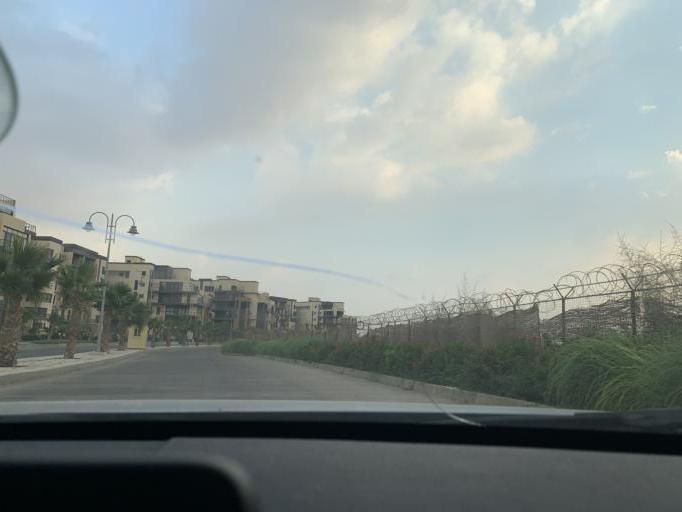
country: EG
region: Muhafazat al Qalyubiyah
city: Al Khankah
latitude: 30.0990
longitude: 31.6563
